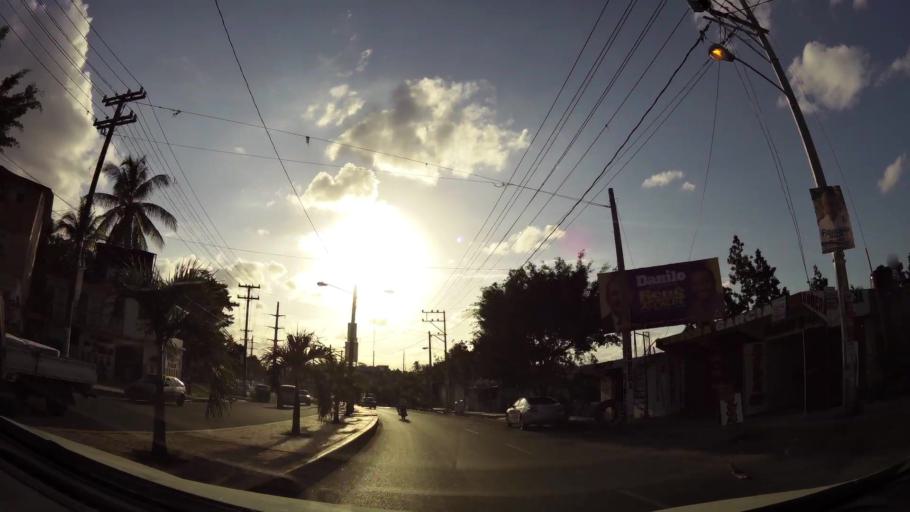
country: DO
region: Nacional
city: La Agustina
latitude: 18.5447
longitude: -69.9281
